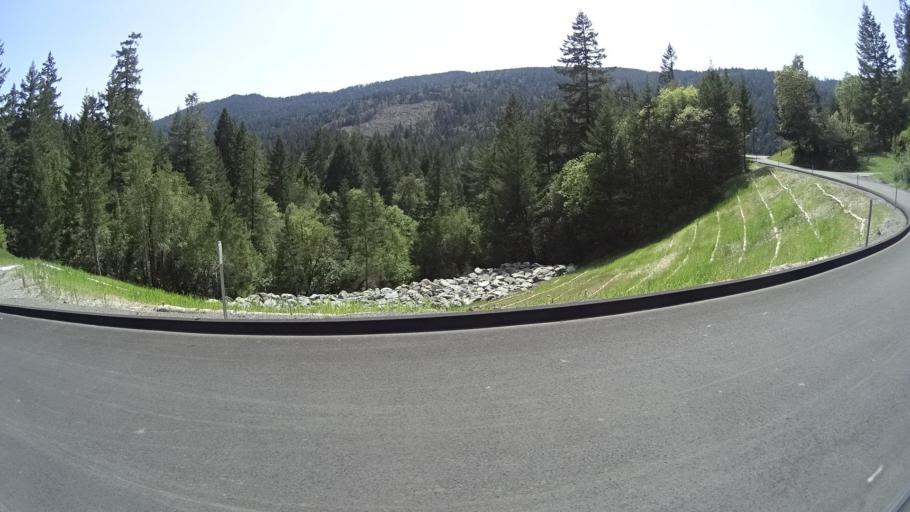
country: US
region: California
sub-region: Humboldt County
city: Redway
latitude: 40.3686
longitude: -123.7308
